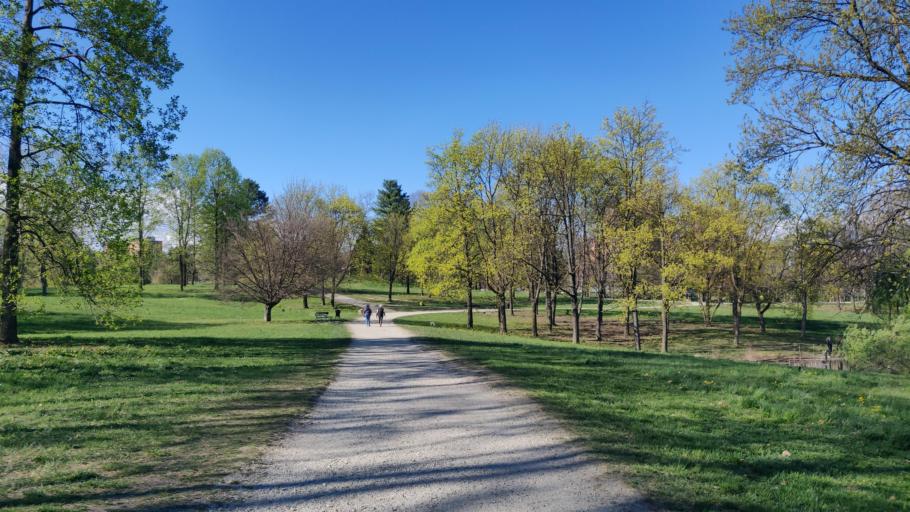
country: IT
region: Piedmont
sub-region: Provincia di Torino
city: Savonera
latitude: 45.0906
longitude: 7.6337
